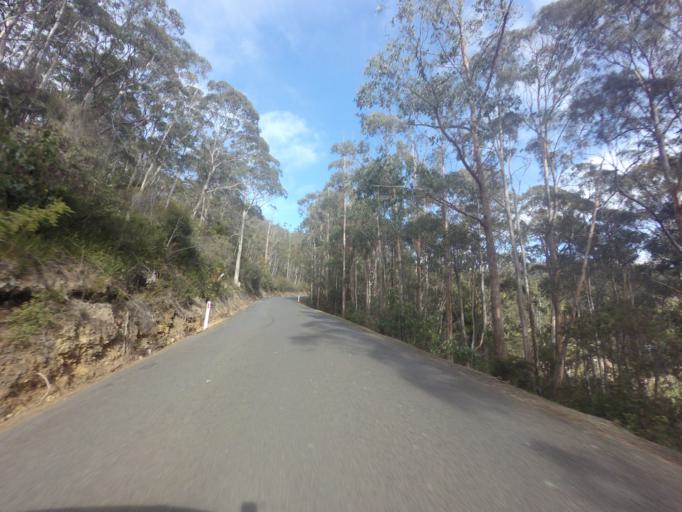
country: AU
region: Tasmania
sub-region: Kingborough
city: Margate
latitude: -43.0017
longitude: 147.1757
